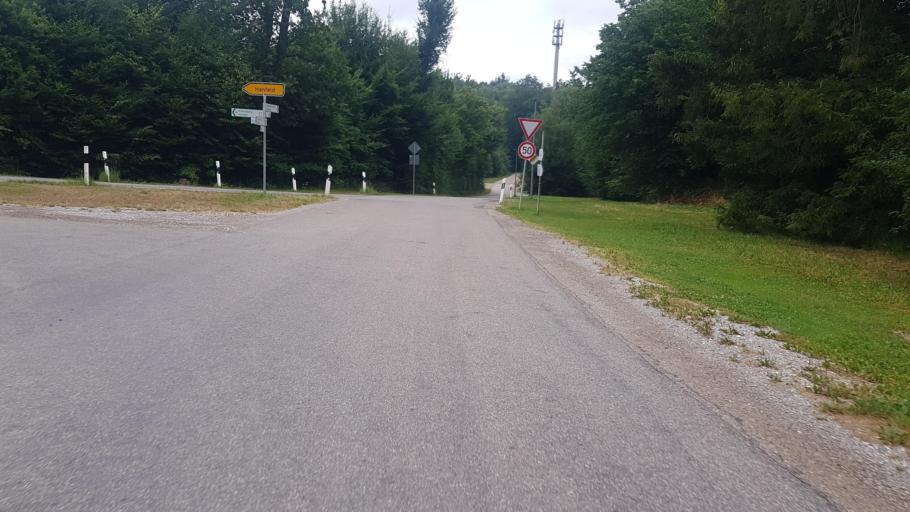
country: DE
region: Bavaria
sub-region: Upper Bavaria
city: Starnberg
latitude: 48.0303
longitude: 11.3519
